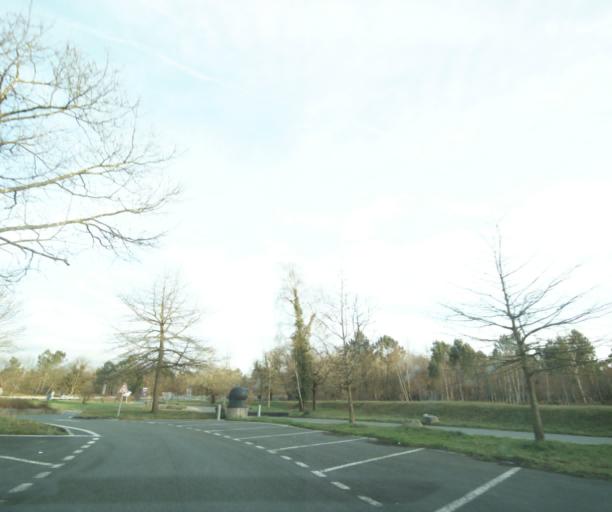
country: FR
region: Aquitaine
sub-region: Departement de la Gironde
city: Reignac
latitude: 45.1878
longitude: -0.4929
